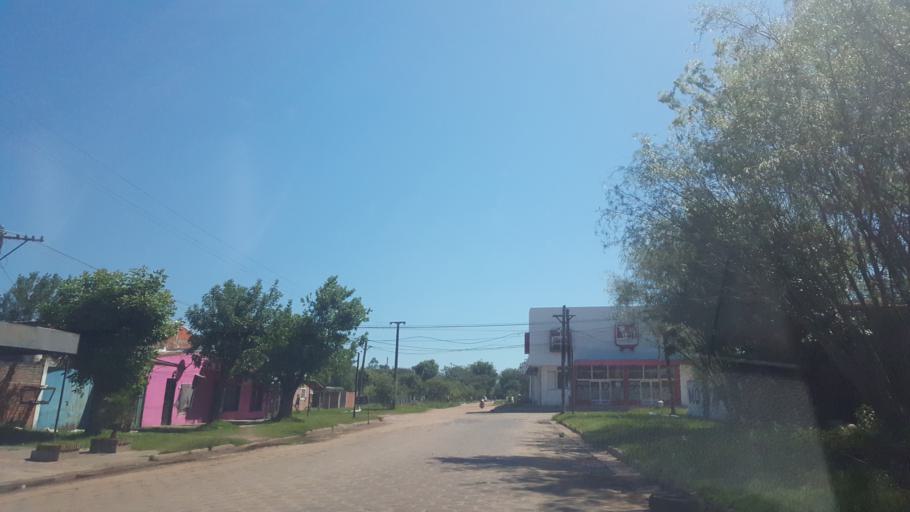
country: AR
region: Corrientes
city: Ituzaingo
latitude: -27.5956
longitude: -56.6962
